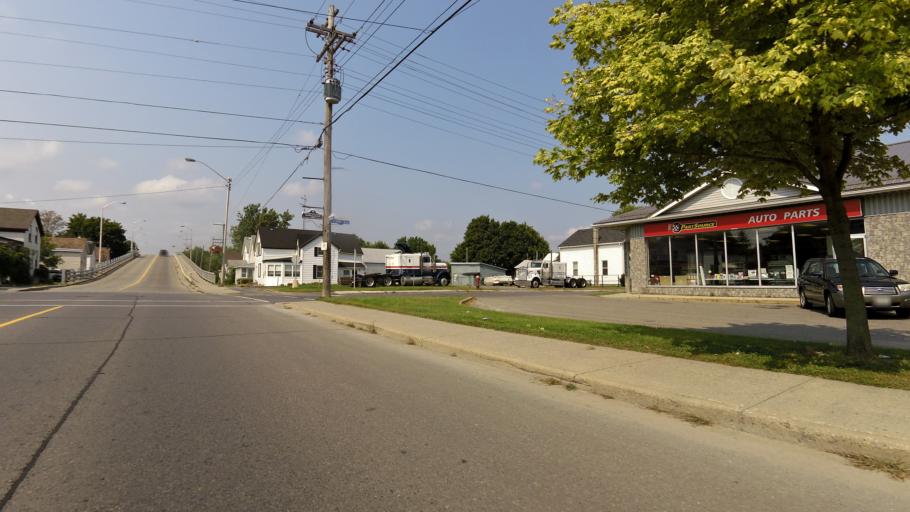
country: CA
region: Ontario
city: Prescott
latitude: 44.7137
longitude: -75.5167
